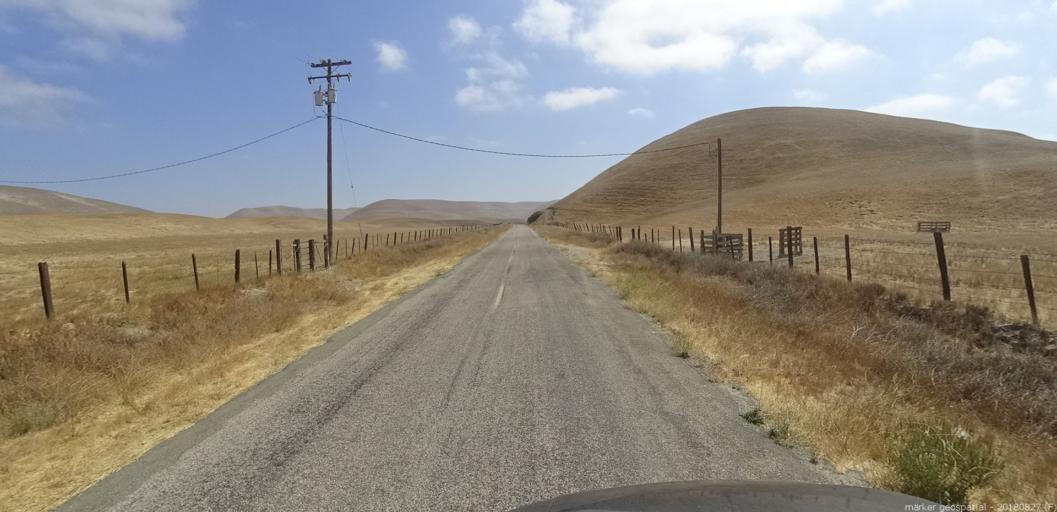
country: US
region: California
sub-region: Monterey County
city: King City
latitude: 36.2299
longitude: -121.0546
